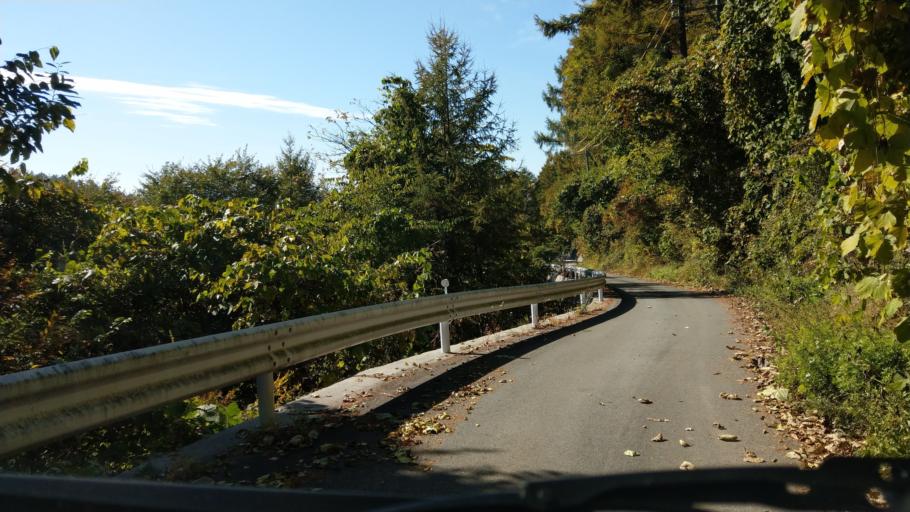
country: JP
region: Nagano
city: Komoro
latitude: 36.3777
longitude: 138.4266
